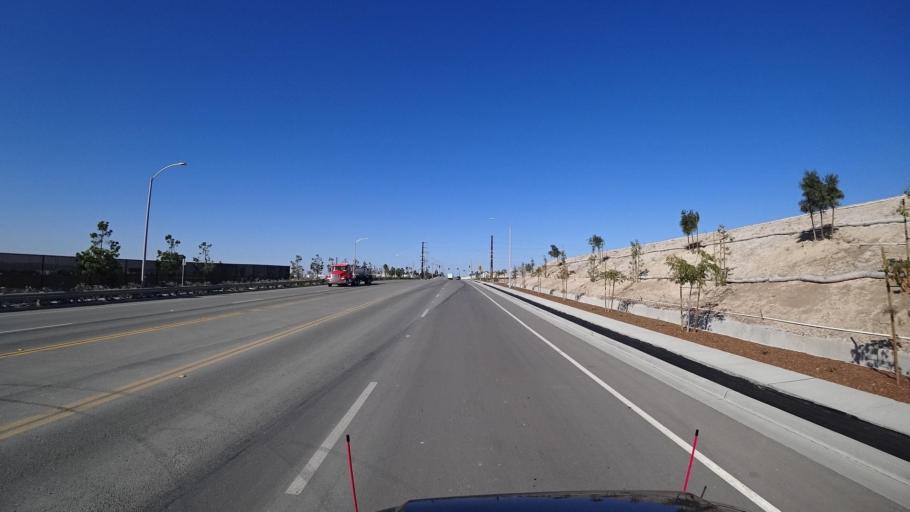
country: MX
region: Baja California
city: Tijuana
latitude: 32.5674
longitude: -116.9168
